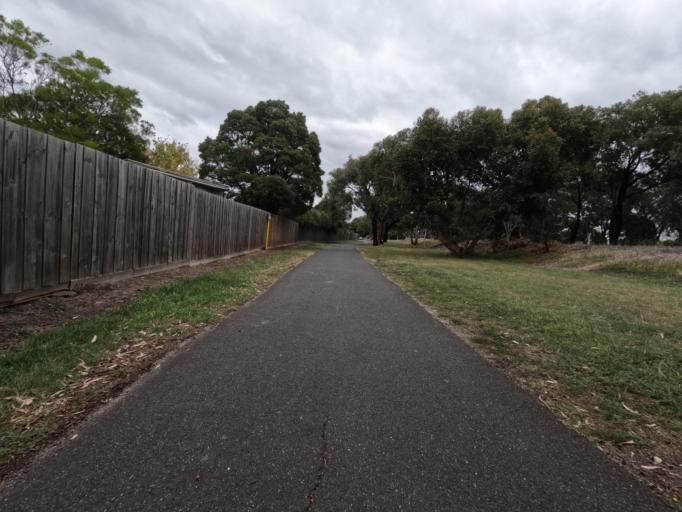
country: AU
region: Victoria
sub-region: Greater Geelong
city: Hamlyn Heights
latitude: -38.1313
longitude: 144.3245
